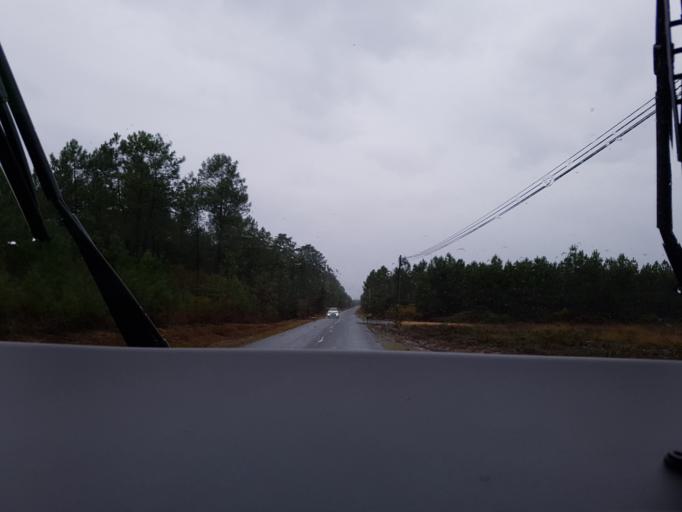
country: FR
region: Aquitaine
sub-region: Departement de la Gironde
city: Saint-Symphorien
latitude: 44.3484
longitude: -0.6170
